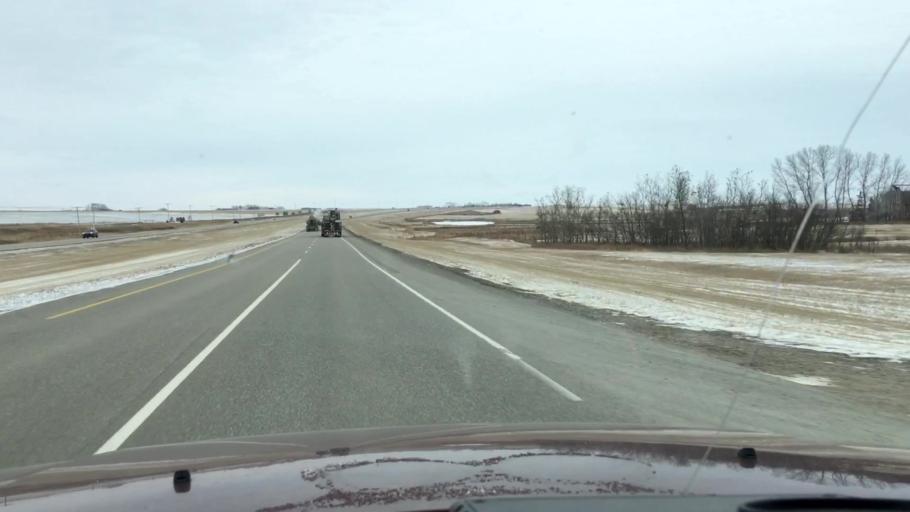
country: CA
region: Saskatchewan
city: Watrous
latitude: 51.2414
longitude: -105.9658
